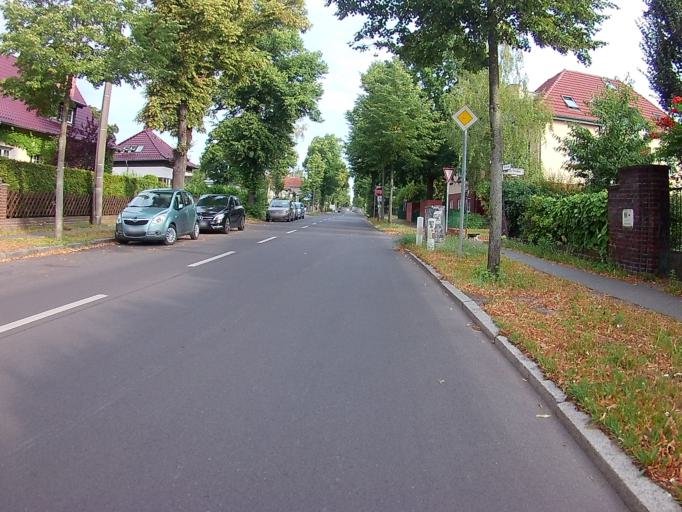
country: DE
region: Berlin
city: Bohnsdorf
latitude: 52.4094
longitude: 13.5584
